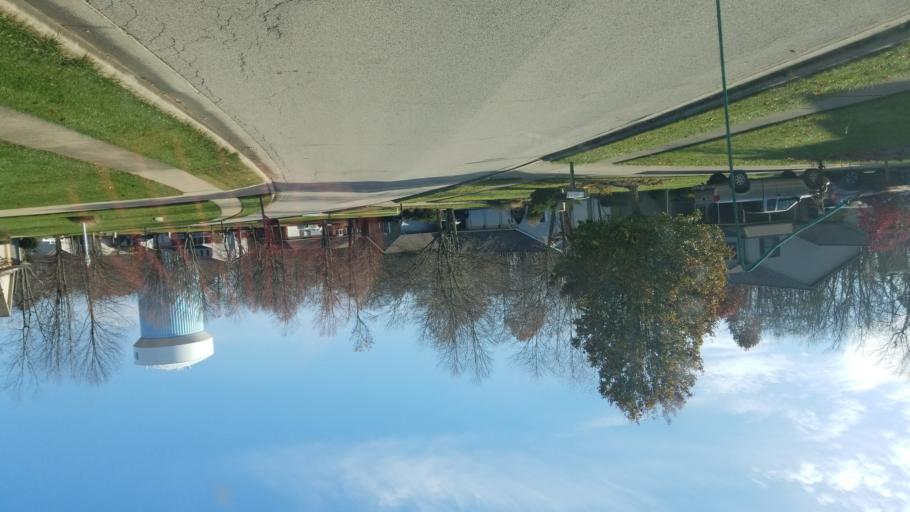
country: US
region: Ohio
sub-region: Richland County
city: Lexington
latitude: 40.7081
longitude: -82.5447
